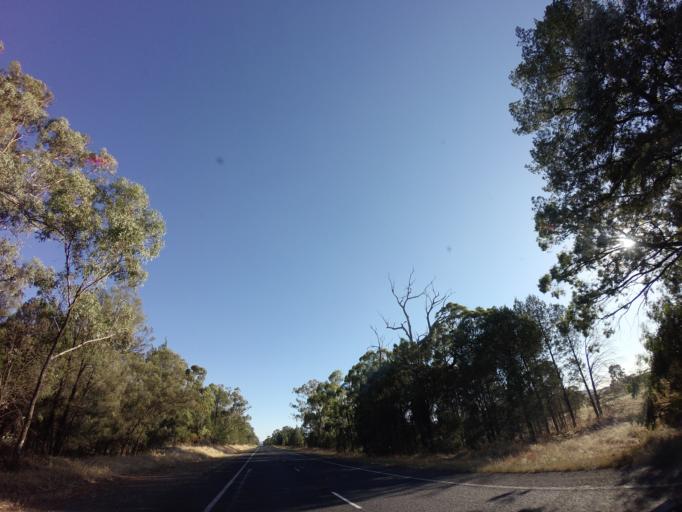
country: AU
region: New South Wales
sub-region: Gilgandra
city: Gilgandra
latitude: -31.5521
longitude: 148.8155
